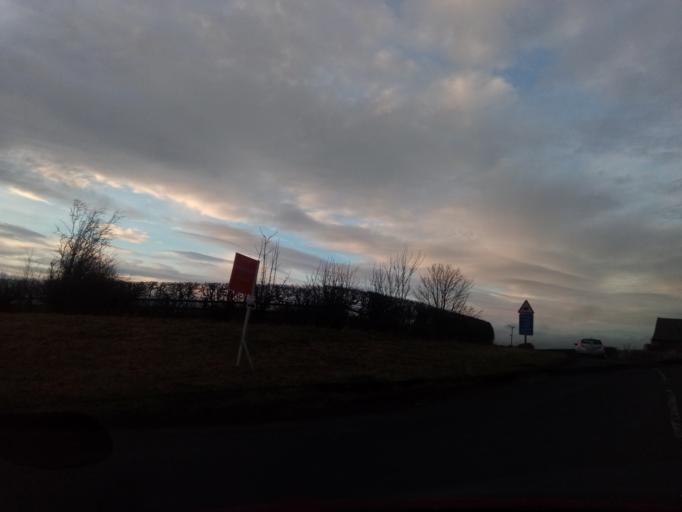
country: GB
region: England
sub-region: Northumberland
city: Ponteland
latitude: 55.0737
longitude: -1.7318
